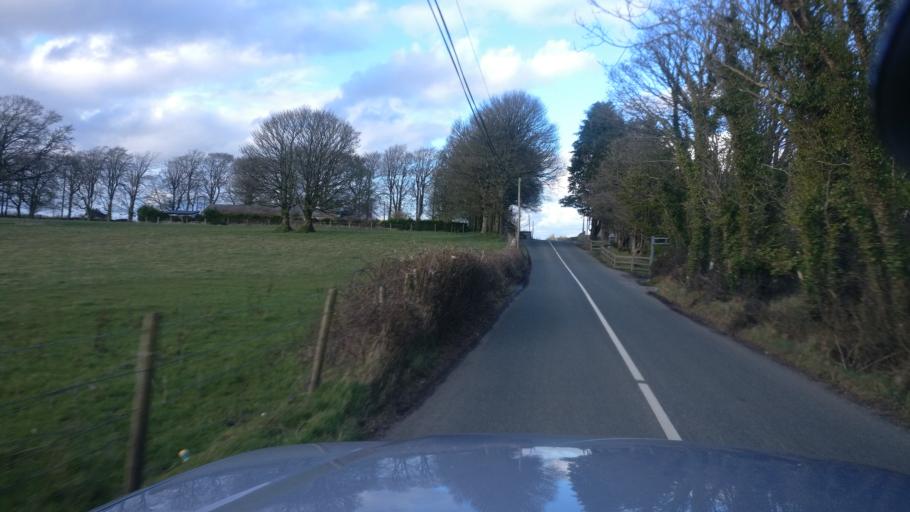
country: IE
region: Connaught
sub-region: County Galway
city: Loughrea
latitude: 53.2193
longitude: -8.3952
